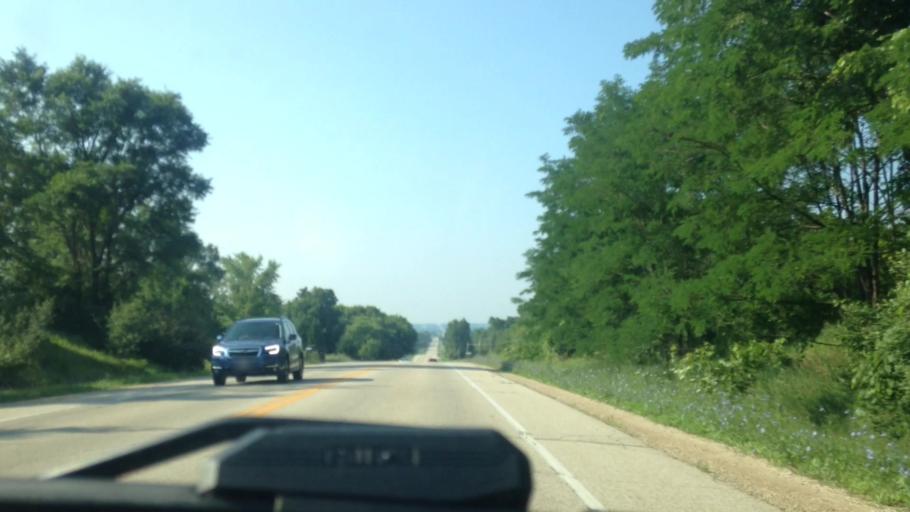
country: US
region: Wisconsin
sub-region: Washington County
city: Slinger
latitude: 43.3027
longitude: -88.2608
